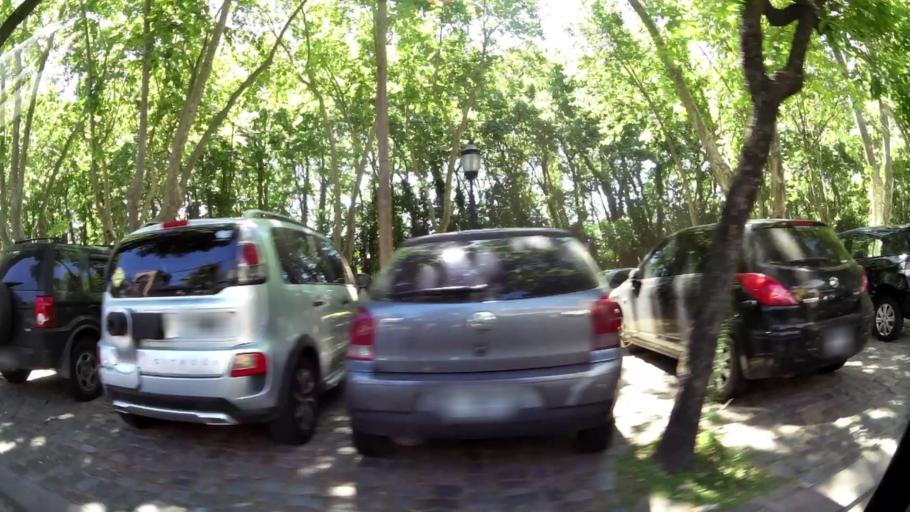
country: AR
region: Buenos Aires
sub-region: Partido de San Isidro
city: San Isidro
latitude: -34.4907
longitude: -58.5264
